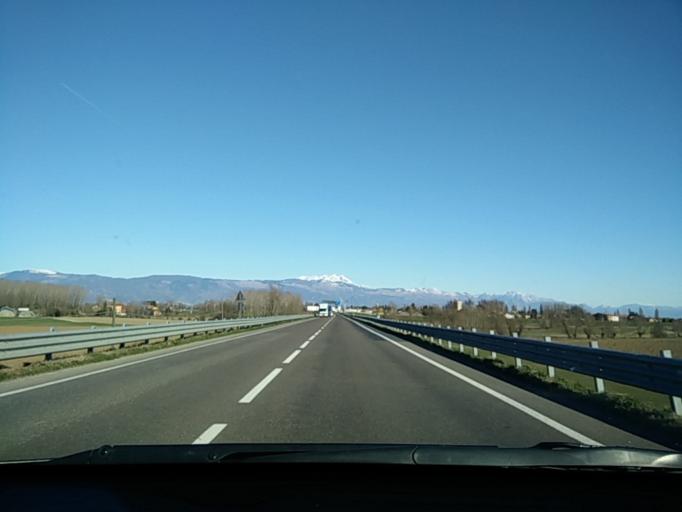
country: IT
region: Veneto
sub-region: Provincia di Treviso
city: Portobuffole
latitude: 45.8462
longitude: 12.5369
